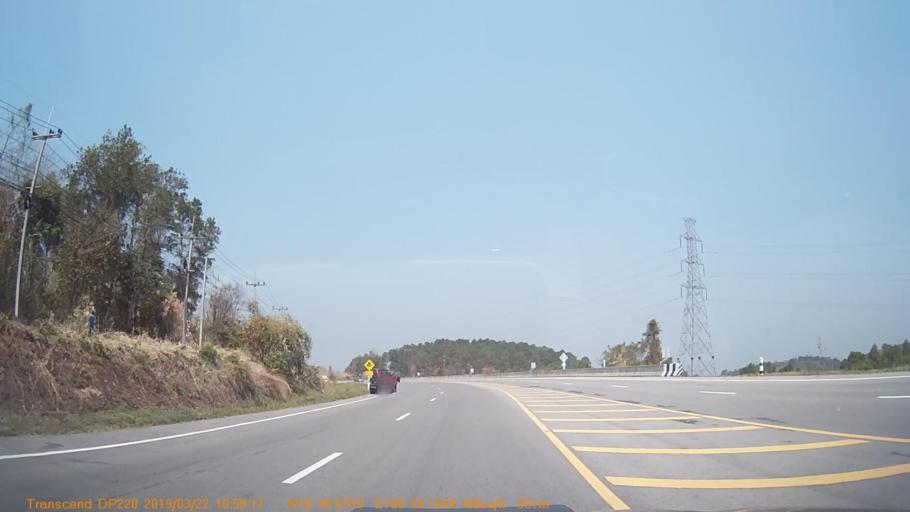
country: TH
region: Phetchabun
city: Khao Kho
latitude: 16.8281
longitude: 100.9182
